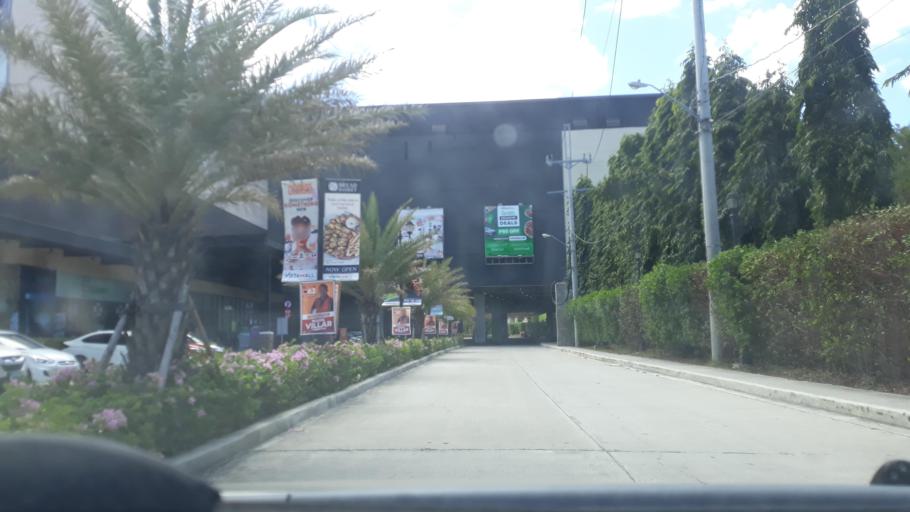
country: PH
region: Calabarzon
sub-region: Province of Cavite
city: Dasmarinas
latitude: 14.3178
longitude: 120.9452
